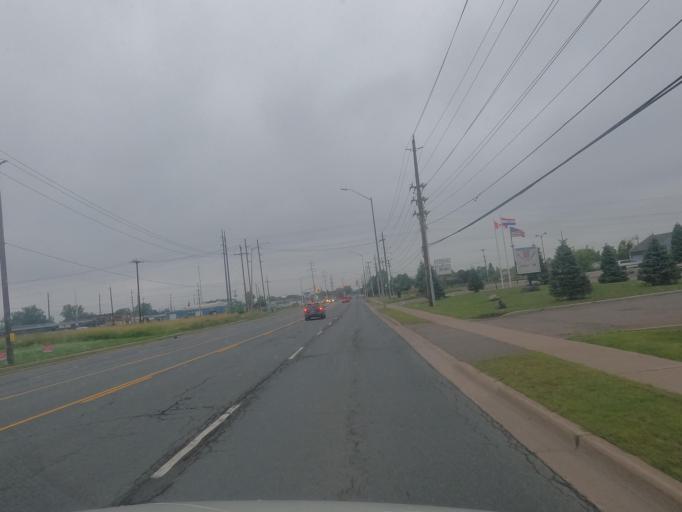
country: CA
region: Ontario
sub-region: Algoma
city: Sault Ste. Marie
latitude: 46.5383
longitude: -84.3274
